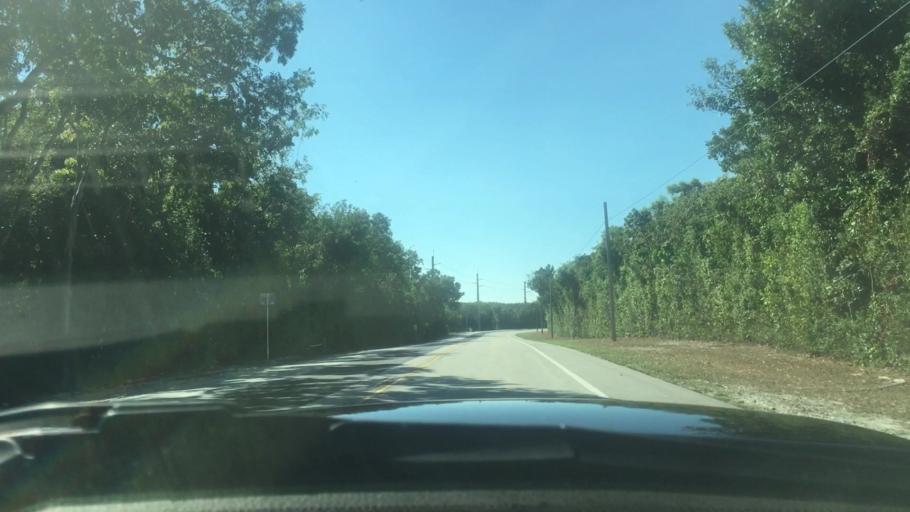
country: US
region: Florida
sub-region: Monroe County
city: North Key Largo
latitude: 25.2294
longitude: -80.3281
